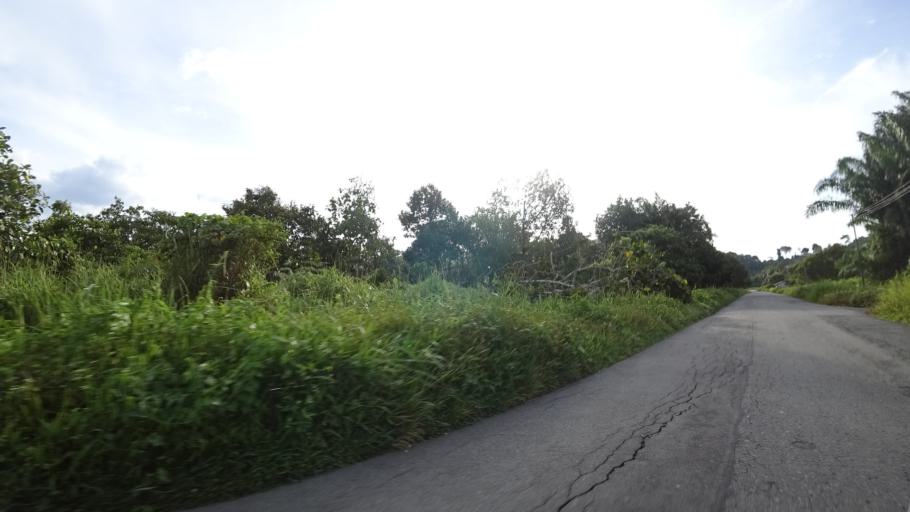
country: BN
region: Tutong
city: Tutong
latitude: 4.8172
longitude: 114.8197
